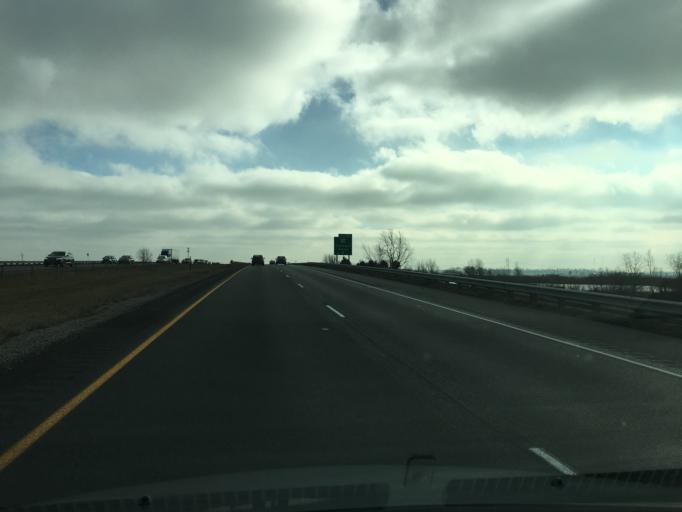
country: US
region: Indiana
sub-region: Clinton County
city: Mulberry
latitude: 40.2677
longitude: -86.6616
